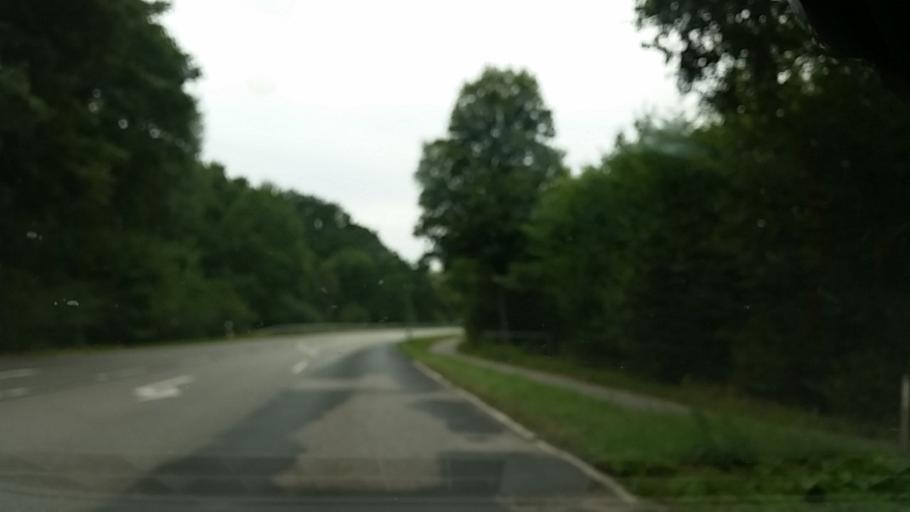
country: DE
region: Schleswig-Holstein
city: Aumuhle
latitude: 53.5299
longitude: 10.3024
